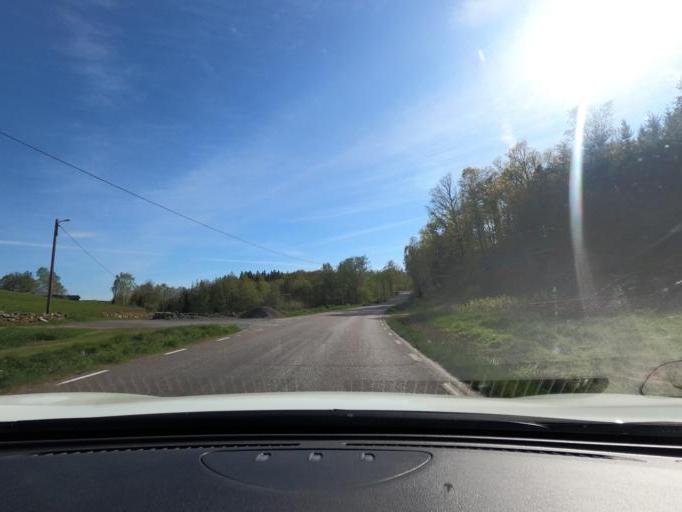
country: SE
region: Vaestra Goetaland
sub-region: Harryda Kommun
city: Landvetter
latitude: 57.6181
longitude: 12.3014
